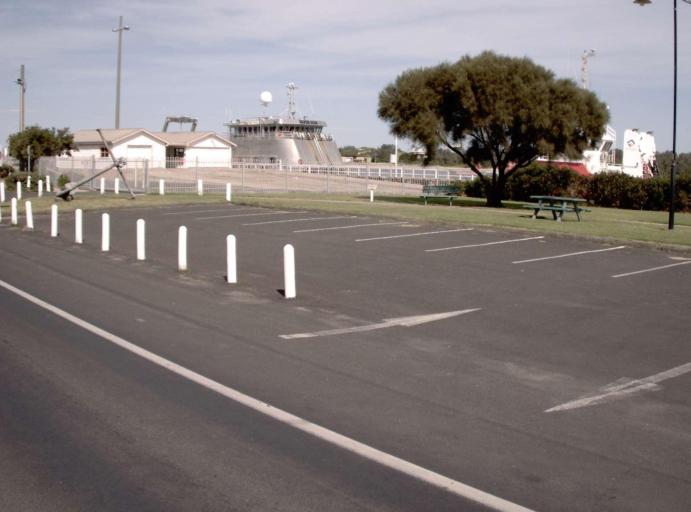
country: AU
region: Victoria
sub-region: East Gippsland
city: Lakes Entrance
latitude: -37.8803
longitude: 147.9888
